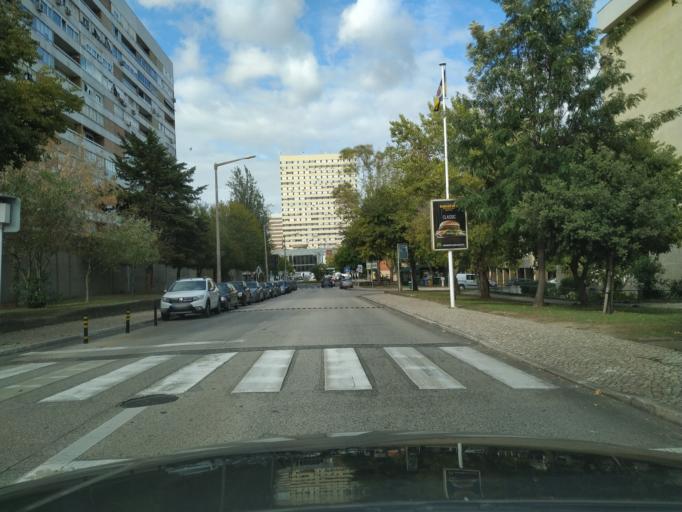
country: PT
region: Lisbon
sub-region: Loures
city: Moscavide
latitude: 38.7800
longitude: -9.1110
